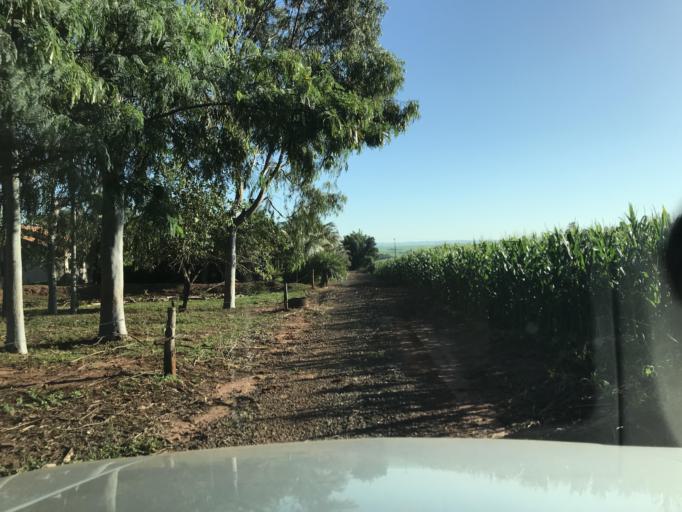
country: BR
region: Parana
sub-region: Palotina
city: Palotina
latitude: -24.2108
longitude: -53.7583
